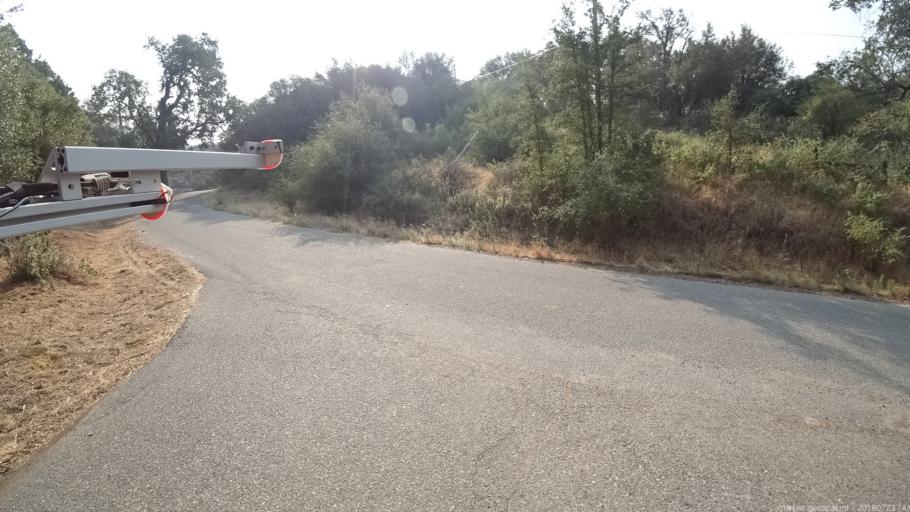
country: US
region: California
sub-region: Madera County
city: Ahwahnee
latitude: 37.3631
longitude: -119.7324
